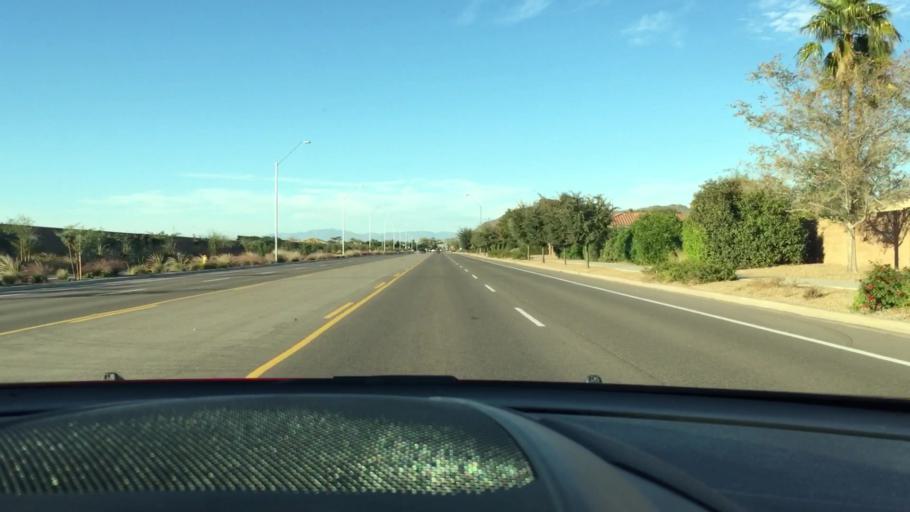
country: US
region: Arizona
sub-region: Maricopa County
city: Sun City West
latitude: 33.6910
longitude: -112.2550
